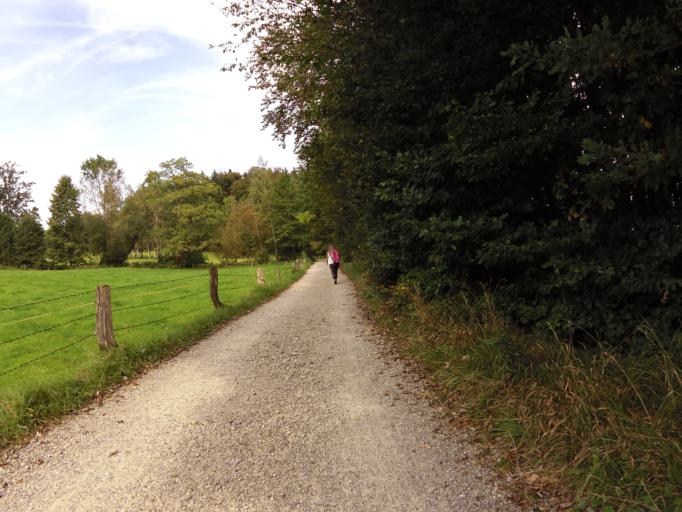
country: DE
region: Bavaria
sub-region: Upper Bavaria
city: Bernried
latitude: 47.8521
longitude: 11.2938
